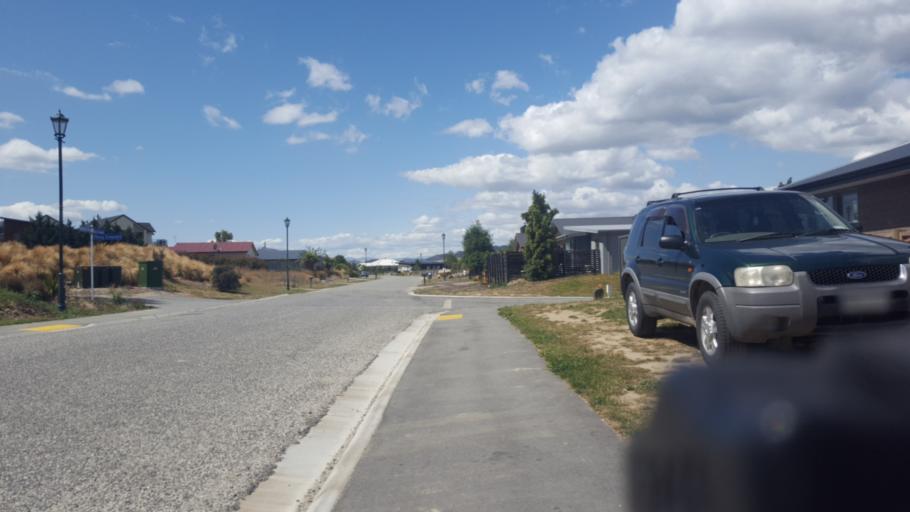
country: NZ
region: Otago
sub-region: Queenstown-Lakes District
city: Wanaka
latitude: -44.9736
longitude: 169.2428
